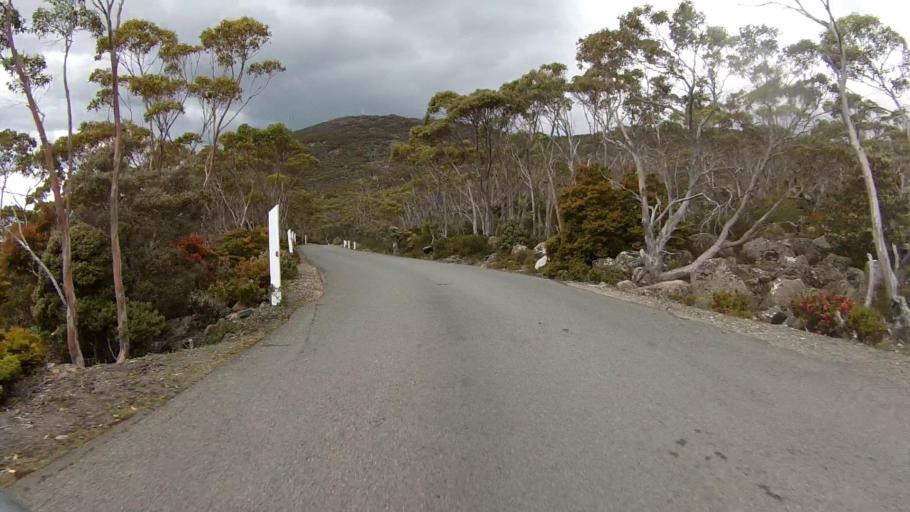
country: AU
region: Tasmania
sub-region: Glenorchy
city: West Moonah
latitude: -42.8864
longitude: 147.2224
